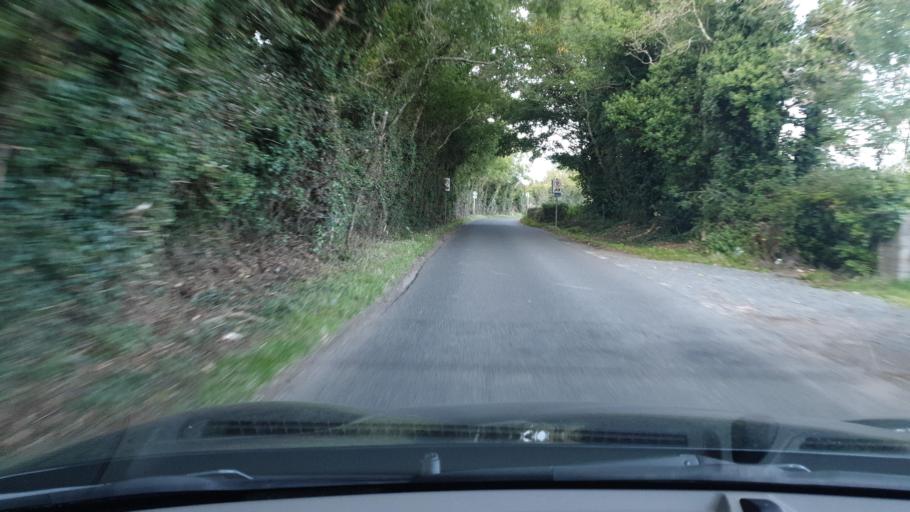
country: IE
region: Leinster
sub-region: South Dublin
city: Newcastle
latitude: 53.2648
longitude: -6.5180
